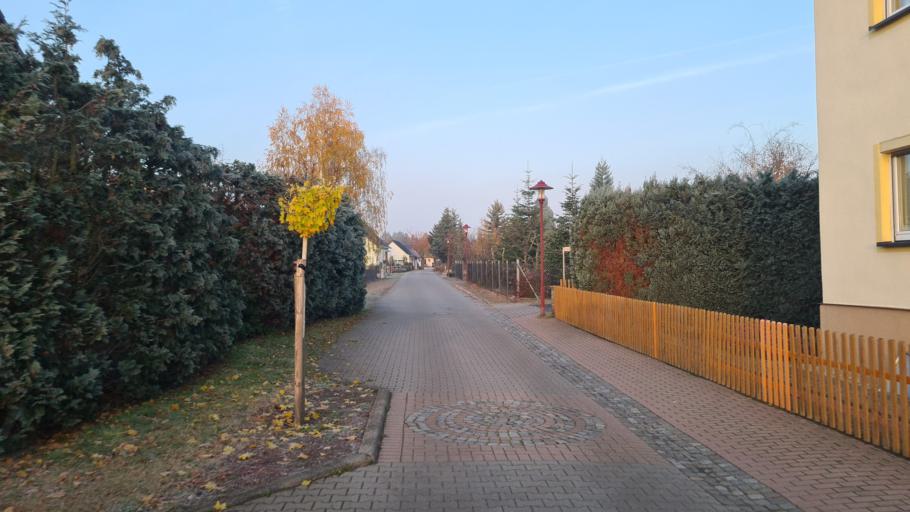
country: DE
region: Saxony-Anhalt
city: Jessen
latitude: 51.7973
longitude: 13.0118
